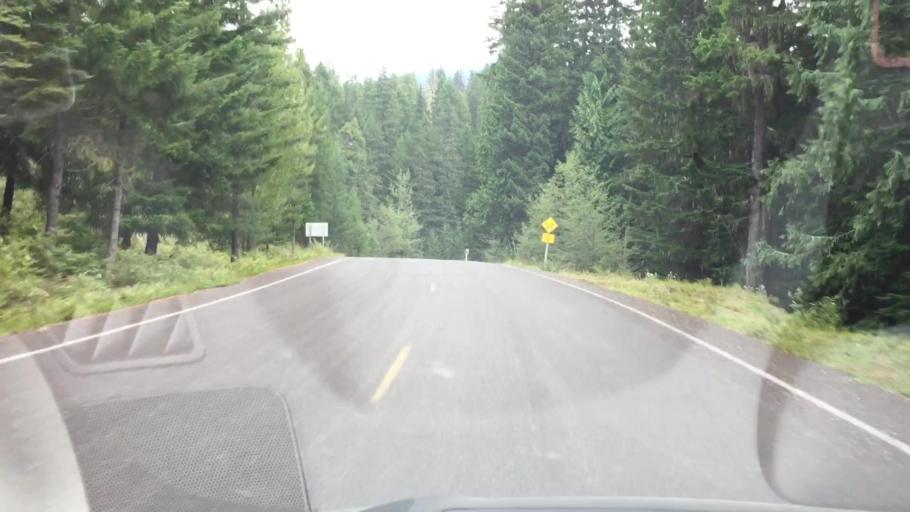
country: US
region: Washington
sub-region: Klickitat County
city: White Salmon
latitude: 46.2322
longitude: -121.6271
